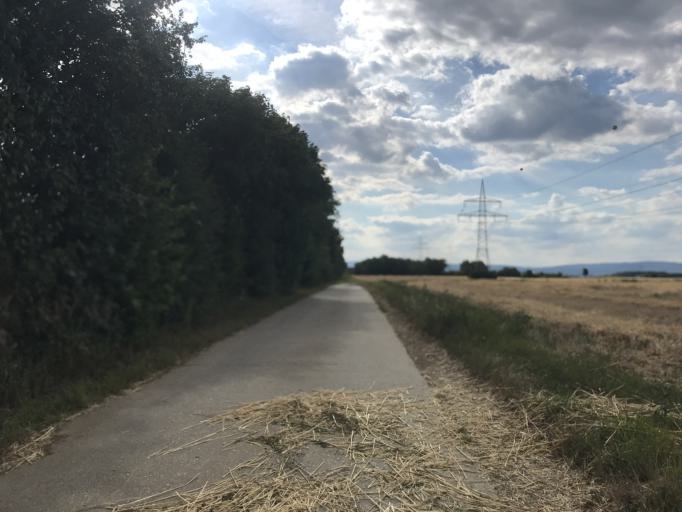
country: DE
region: Hesse
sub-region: Regierungsbezirk Darmstadt
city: Hochheim am Main
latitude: 50.0256
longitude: 8.3200
